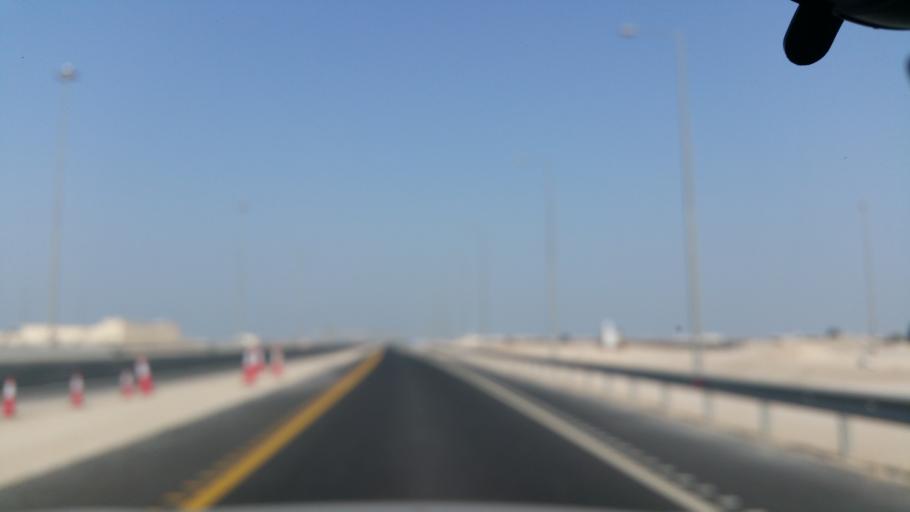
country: QA
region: Baladiyat Umm Salal
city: Umm Salal `Ali
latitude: 25.4495
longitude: 51.4164
